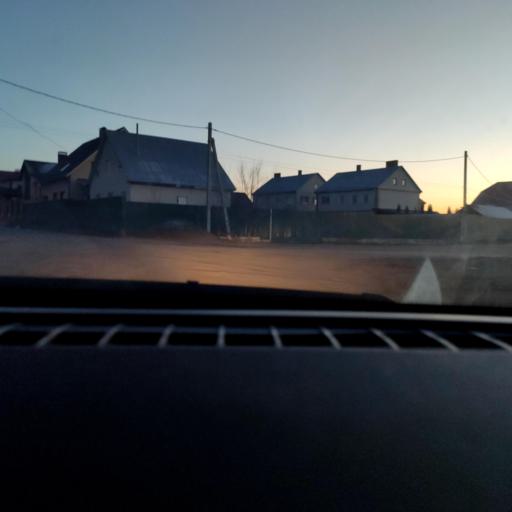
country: RU
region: Voronezj
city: Podgornoye
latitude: 51.7446
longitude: 39.1612
